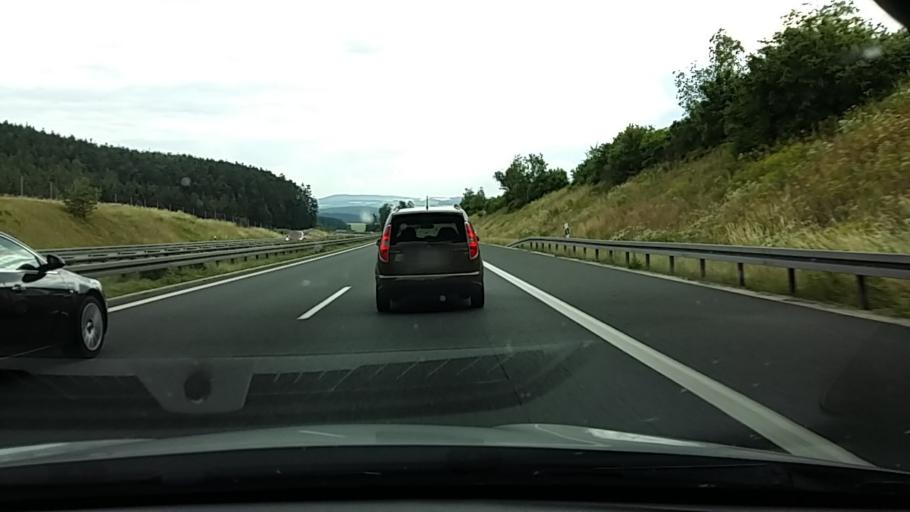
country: DE
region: Bavaria
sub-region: Upper Palatinate
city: Wernberg-Koblitz
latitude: 49.5619
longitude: 12.2048
